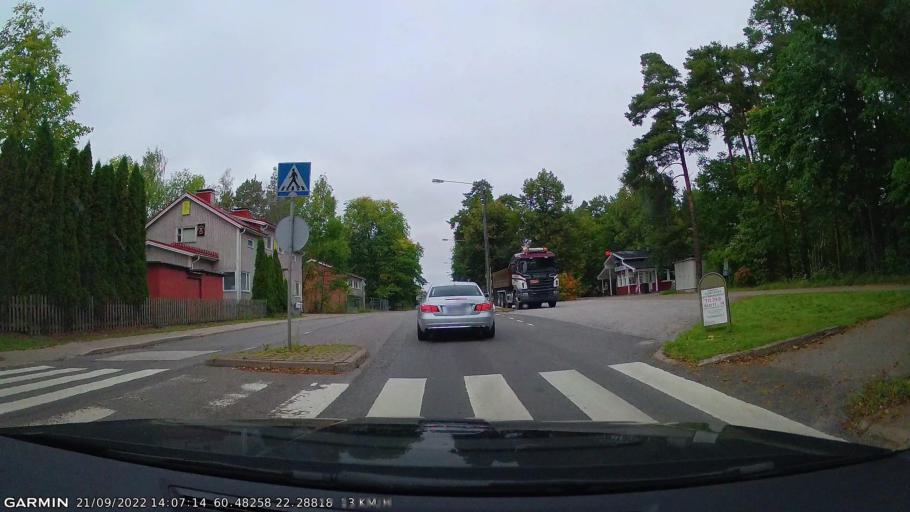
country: FI
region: Varsinais-Suomi
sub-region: Turku
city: Turku
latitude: 60.4826
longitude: 22.2880
